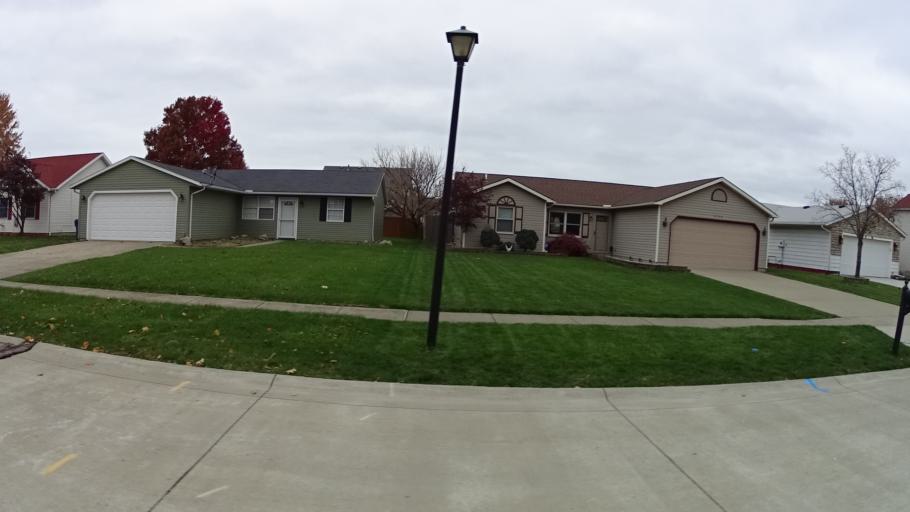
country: US
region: Ohio
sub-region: Lorain County
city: Lorain
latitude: 41.4351
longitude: -82.2108
